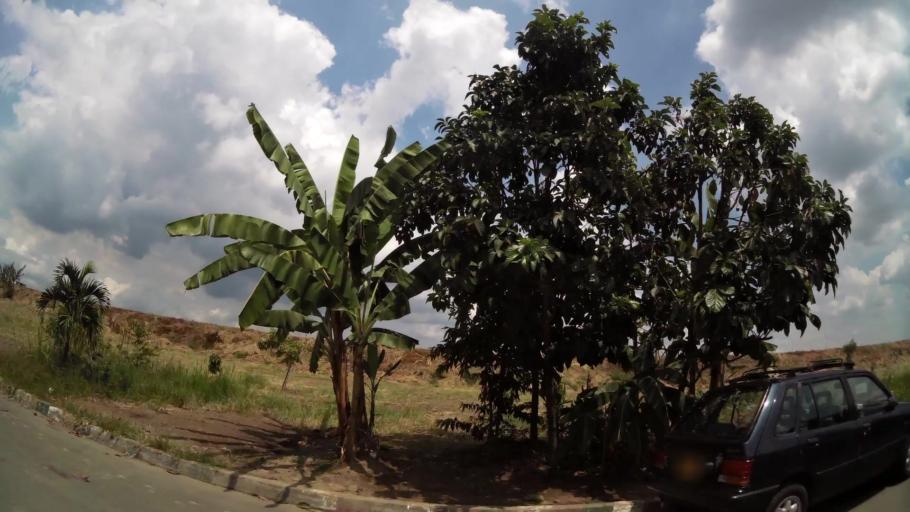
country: CO
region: Valle del Cauca
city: Cali
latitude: 3.4569
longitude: -76.4618
